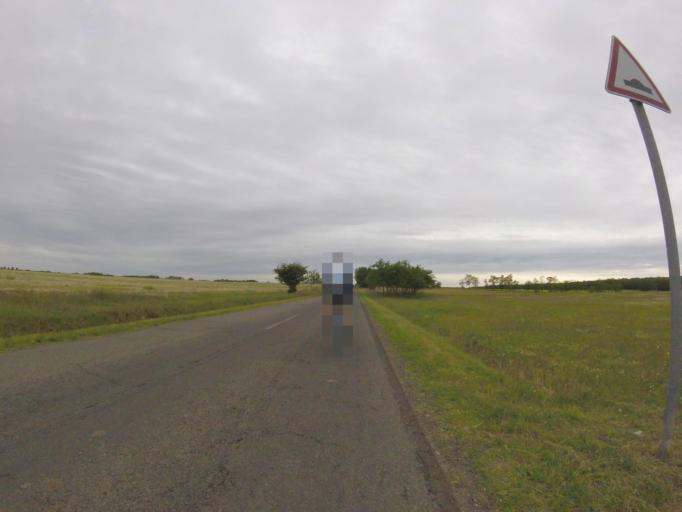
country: HU
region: Pest
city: Inarcs
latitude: 47.2677
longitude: 19.3120
